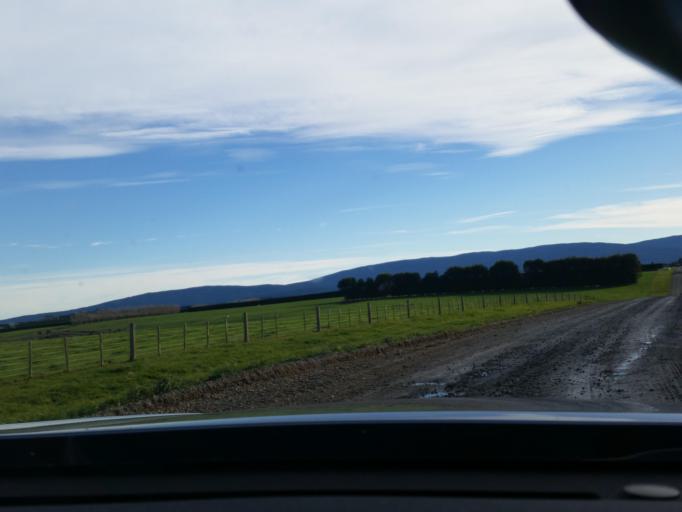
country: NZ
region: Southland
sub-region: Southland District
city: Riverton
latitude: -46.2791
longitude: 168.0523
